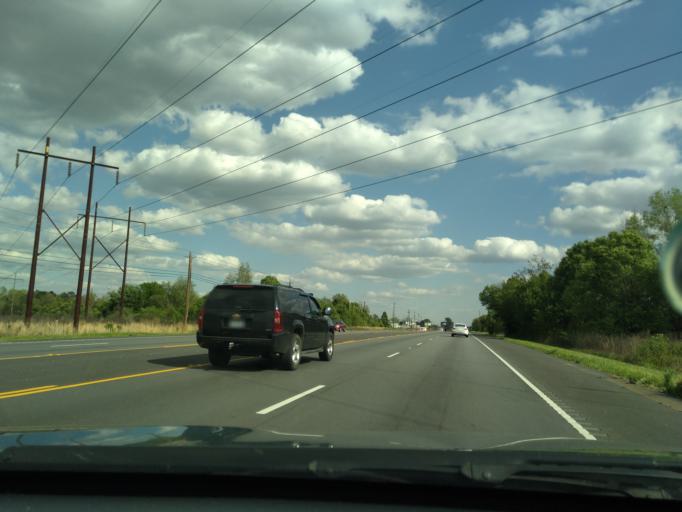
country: US
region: South Carolina
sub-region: Florence County
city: Florence
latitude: 34.2191
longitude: -79.7863
